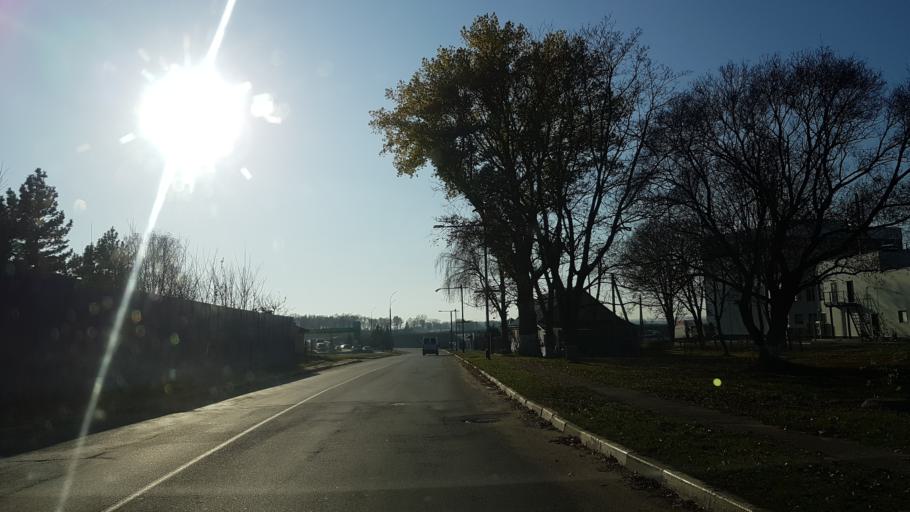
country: BY
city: Fanipol
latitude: 53.7375
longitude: 27.3109
